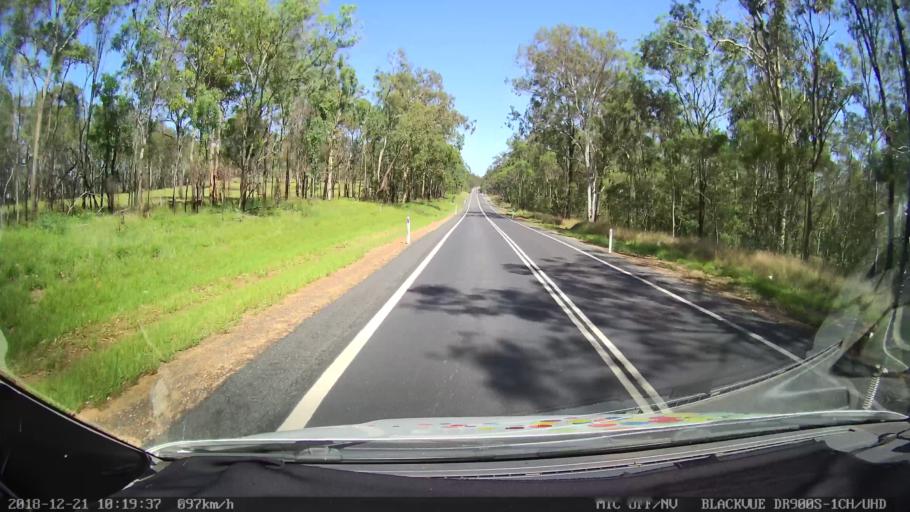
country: AU
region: New South Wales
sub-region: Clarence Valley
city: South Grafton
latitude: -29.6739
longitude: 152.8394
